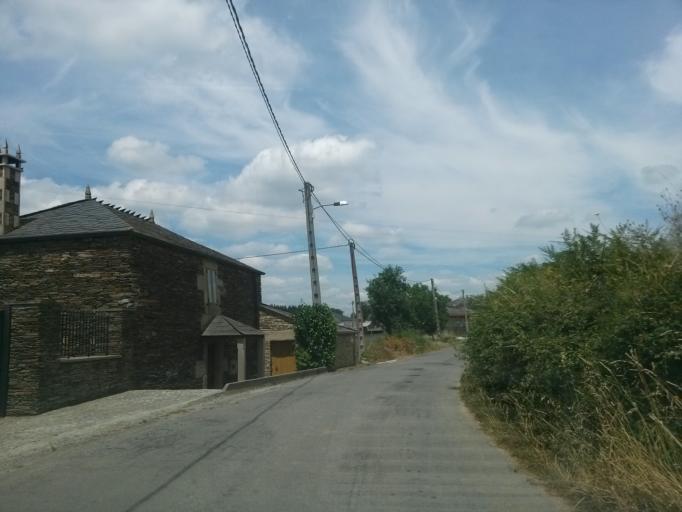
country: ES
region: Galicia
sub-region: Provincia de Lugo
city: Lugo
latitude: 43.0386
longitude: -7.6081
